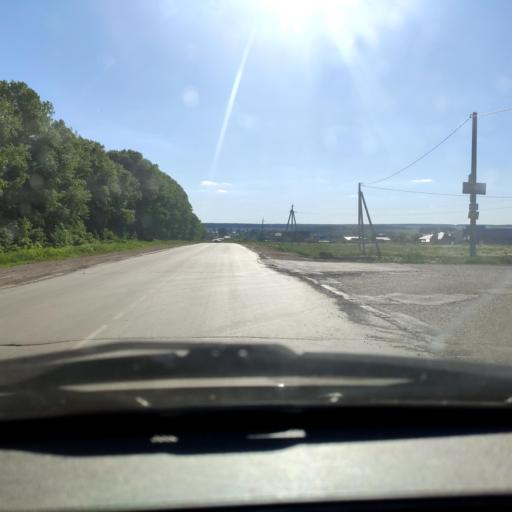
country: RU
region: Bashkortostan
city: Asanovo
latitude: 54.8163
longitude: 55.5934
